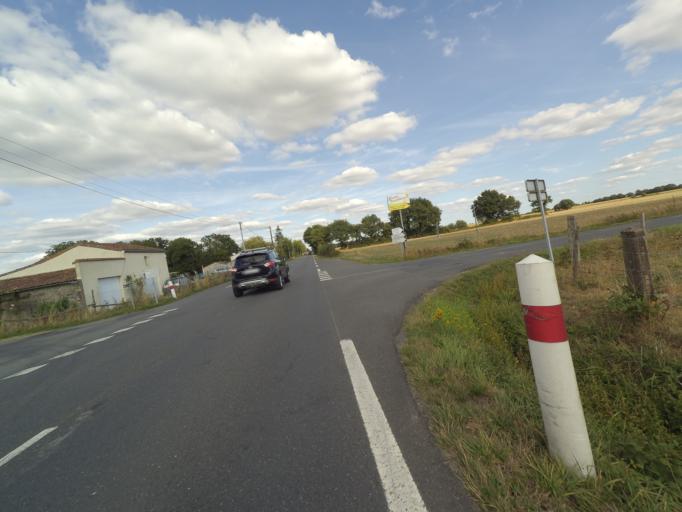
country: FR
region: Pays de la Loire
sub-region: Departement de la Loire-Atlantique
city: Vieillevigne
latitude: 46.9724
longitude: -1.3883
